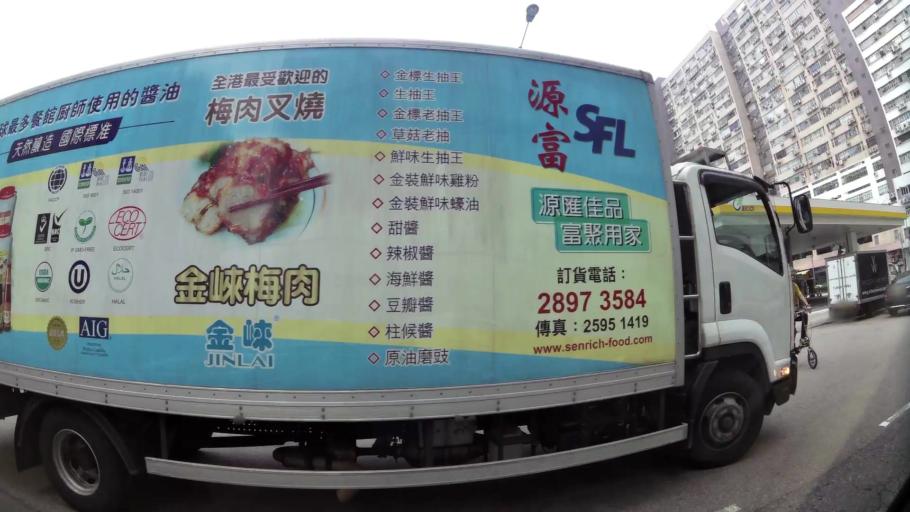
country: HK
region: Wanchai
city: Wan Chai
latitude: 22.2672
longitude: 114.2454
